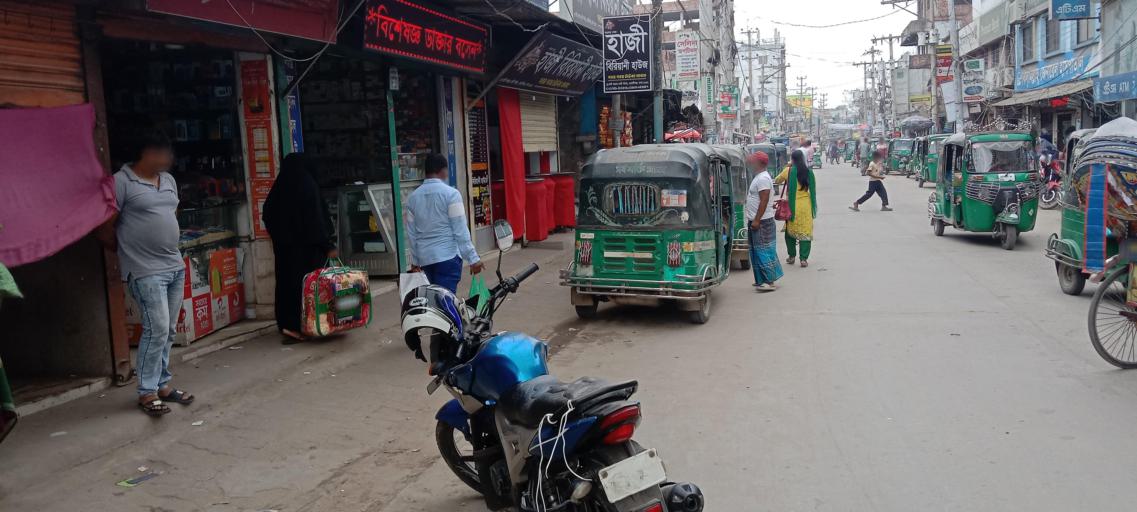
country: BD
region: Dhaka
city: Azimpur
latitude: 23.7301
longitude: 90.3348
